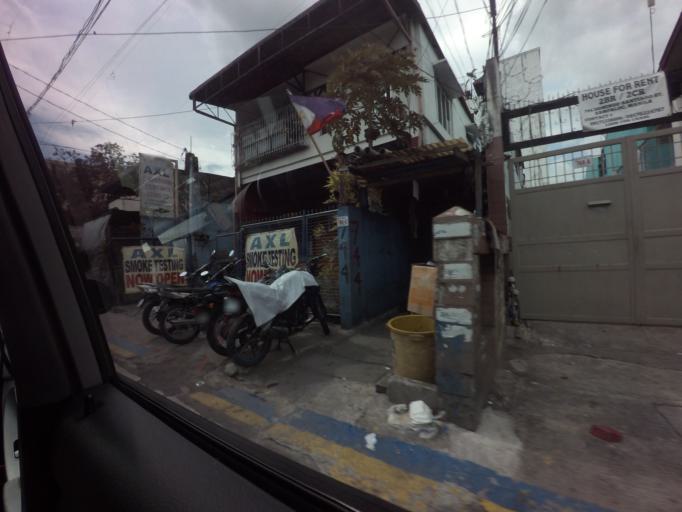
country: PH
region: Metro Manila
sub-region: City of Manila
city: Quiapo
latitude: 14.6039
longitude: 121.0069
